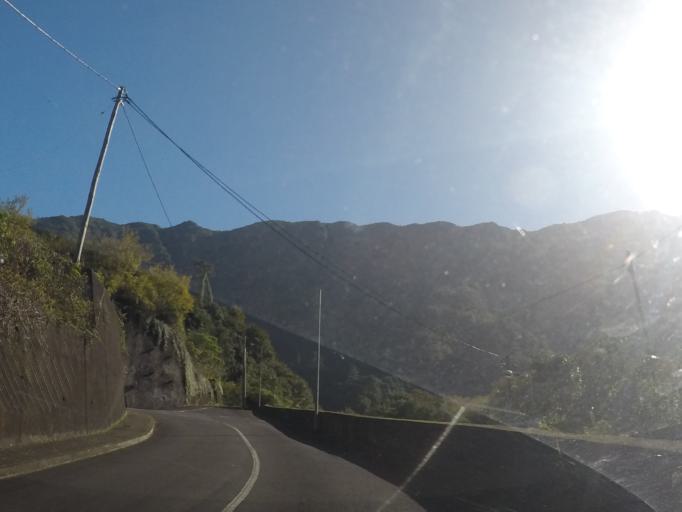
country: PT
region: Madeira
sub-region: Sao Vicente
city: Sao Vicente
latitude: 32.8003
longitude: -16.9638
